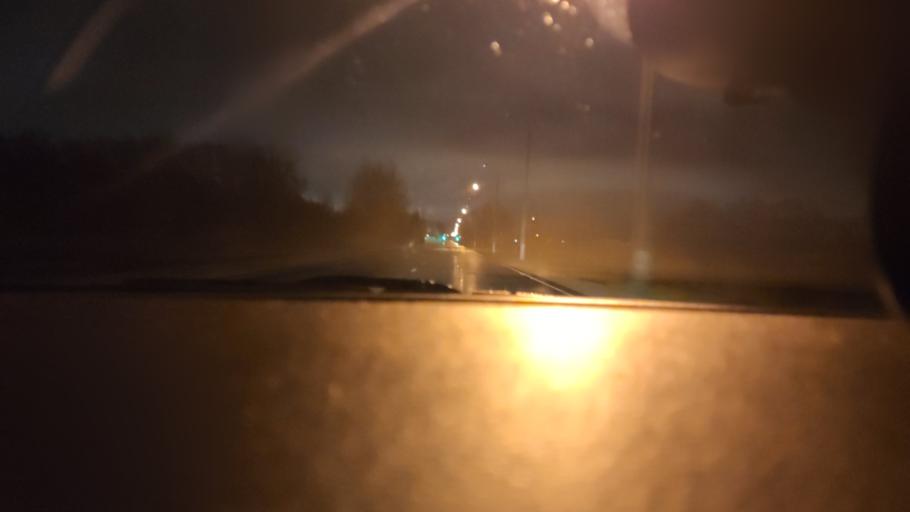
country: RU
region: Perm
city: Kondratovo
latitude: 57.9826
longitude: 56.1319
